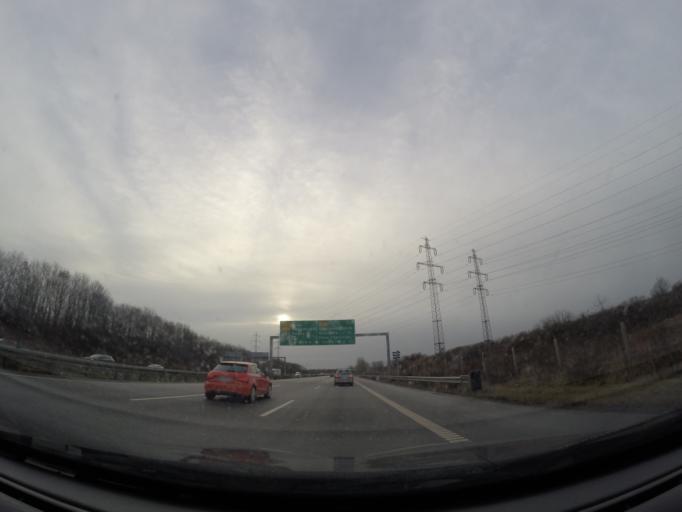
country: DK
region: Capital Region
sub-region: Hoje-Taastrup Kommune
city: Taastrup
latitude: 55.6740
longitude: 12.3221
